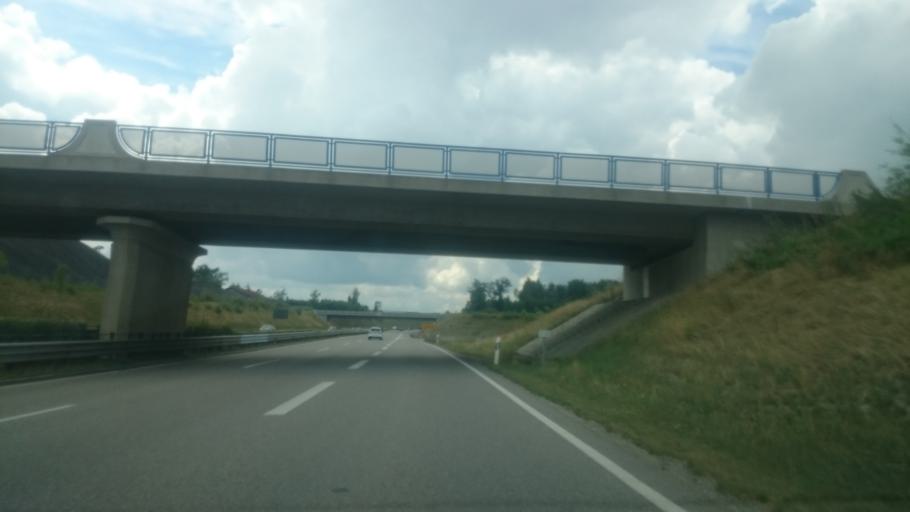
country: DE
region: Bavaria
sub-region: Upper Bavaria
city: Hurlach
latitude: 48.0784
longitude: 10.8306
